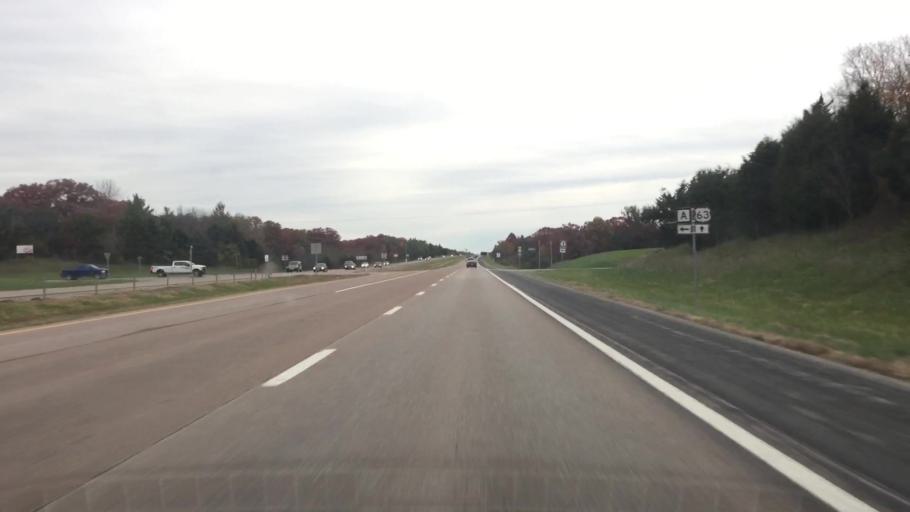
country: US
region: Missouri
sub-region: Boone County
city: Ashland
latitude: 38.7298
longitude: -92.2539
